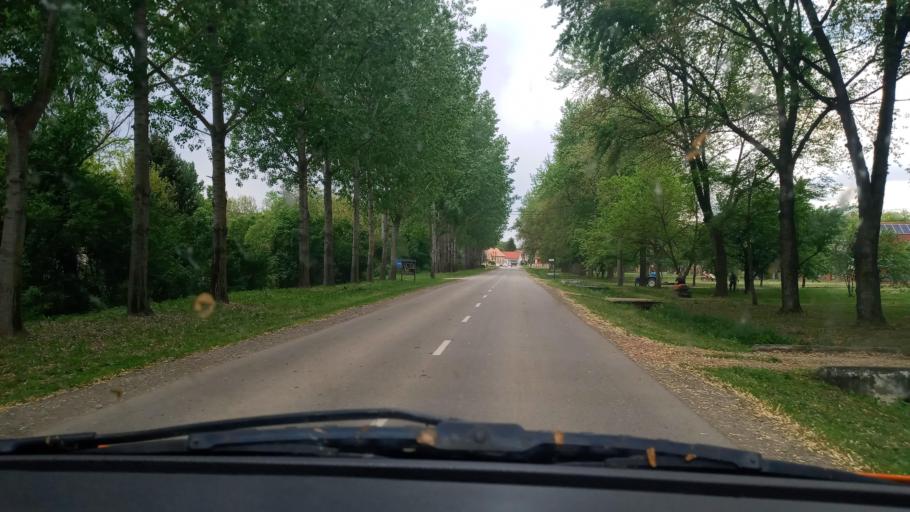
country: HU
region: Baranya
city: Villany
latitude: 45.8434
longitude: 18.4897
